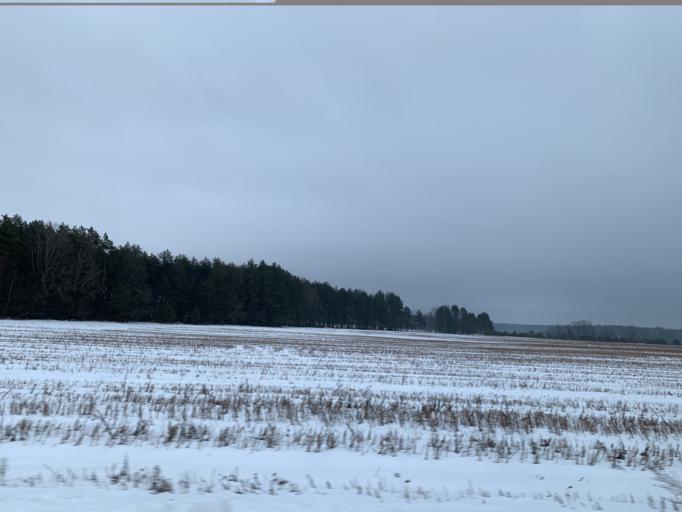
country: BY
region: Minsk
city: Il'ya
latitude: 54.5525
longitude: 27.2846
